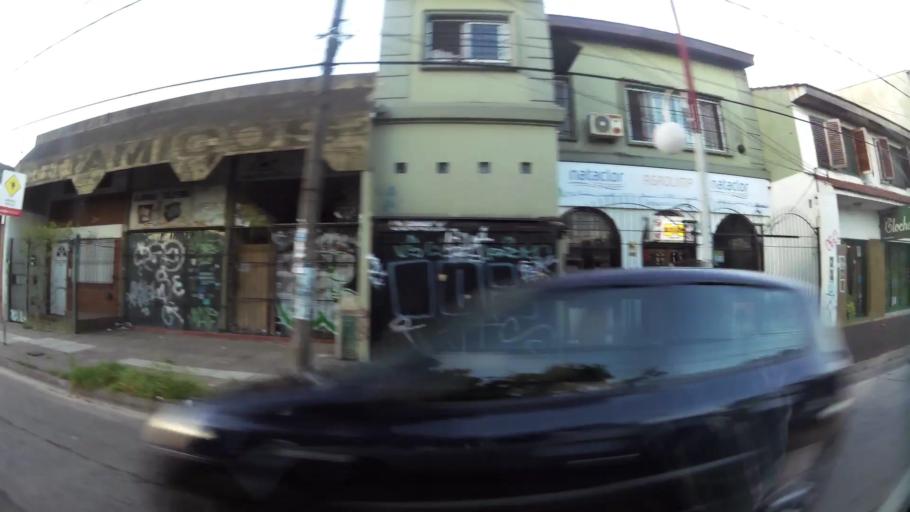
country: AR
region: Buenos Aires
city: Ituzaingo
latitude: -34.6487
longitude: -58.6565
